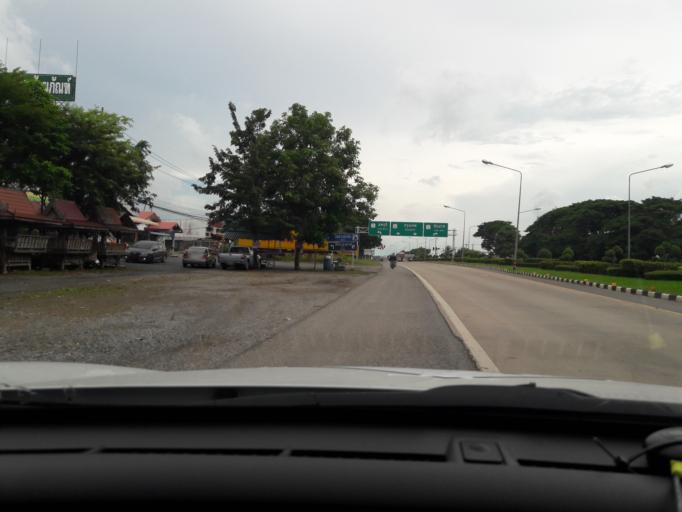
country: TH
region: Nakhon Sawan
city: Tak Fa
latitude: 15.3543
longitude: 100.5027
